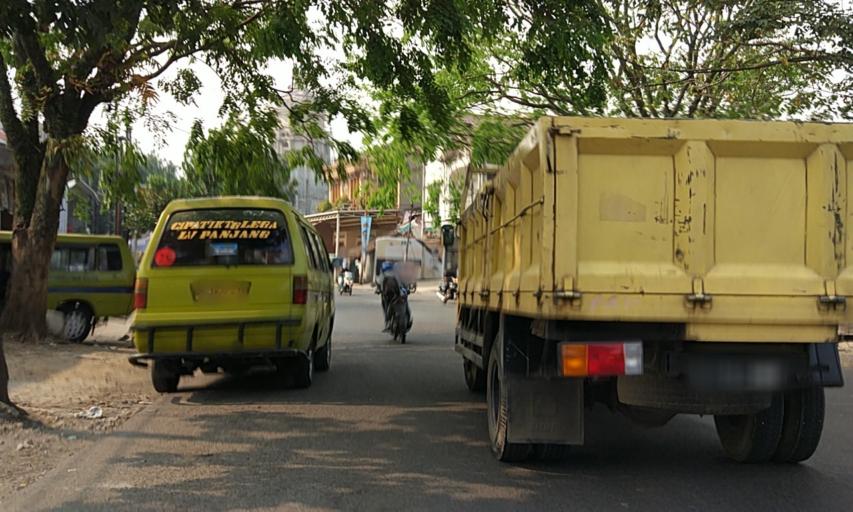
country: ID
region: West Java
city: Margahayukencana
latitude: -6.9507
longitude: 107.5651
